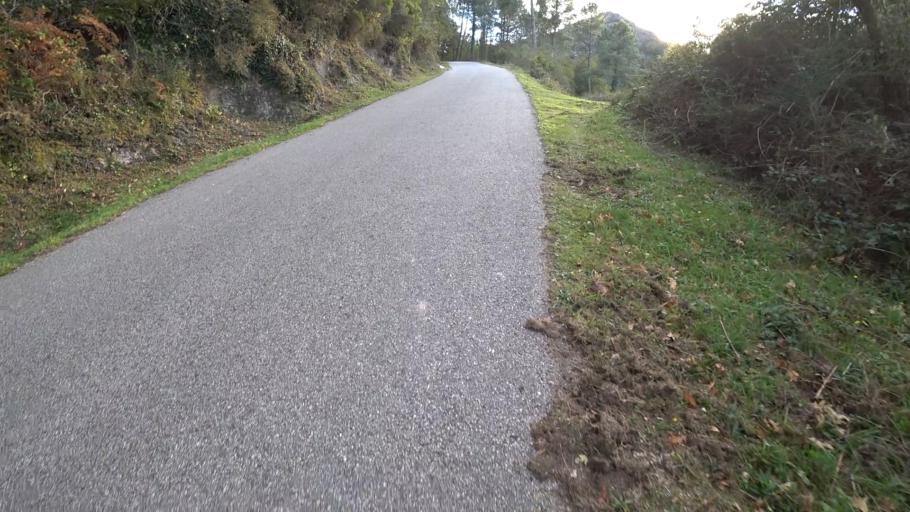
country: PT
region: Braga
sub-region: Terras de Bouro
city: Antas
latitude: 41.7633
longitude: -8.1991
